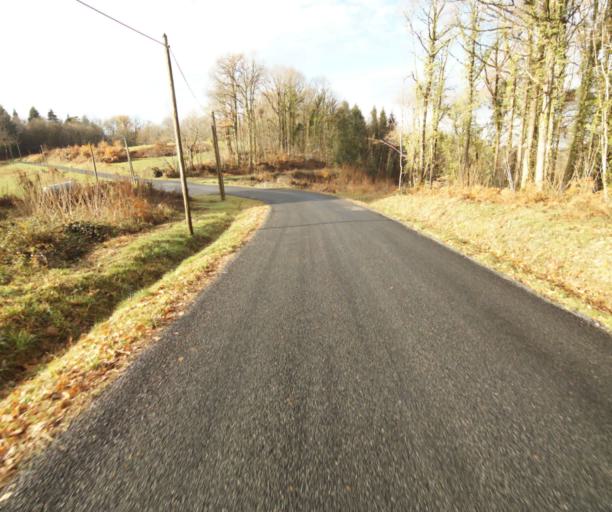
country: FR
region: Limousin
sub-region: Departement de la Correze
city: Sainte-Fereole
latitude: 45.2671
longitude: 1.5927
